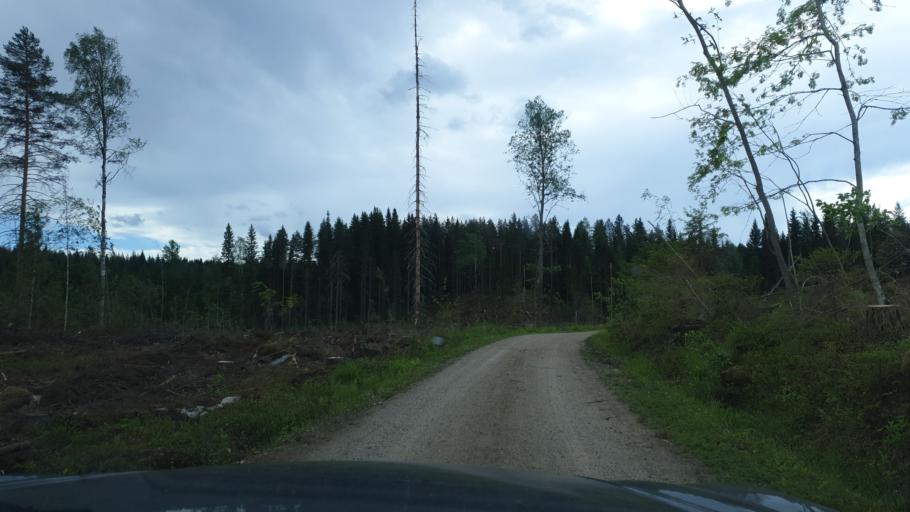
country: FI
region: Northern Savo
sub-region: Koillis-Savo
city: Kaavi
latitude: 62.9802
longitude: 28.7564
